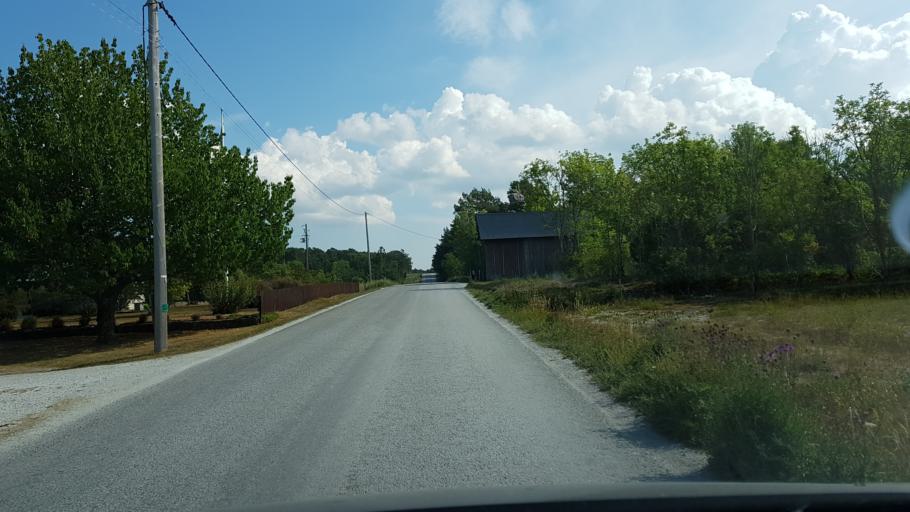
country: SE
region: Gotland
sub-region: Gotland
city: Visby
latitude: 57.8213
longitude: 18.5171
